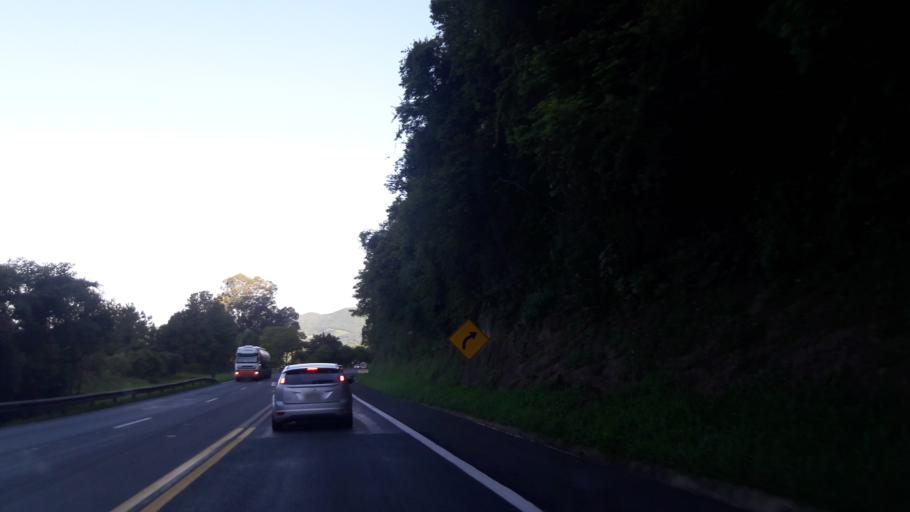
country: BR
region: Parana
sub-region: Prudentopolis
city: Prudentopolis
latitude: -25.3154
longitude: -51.1988
